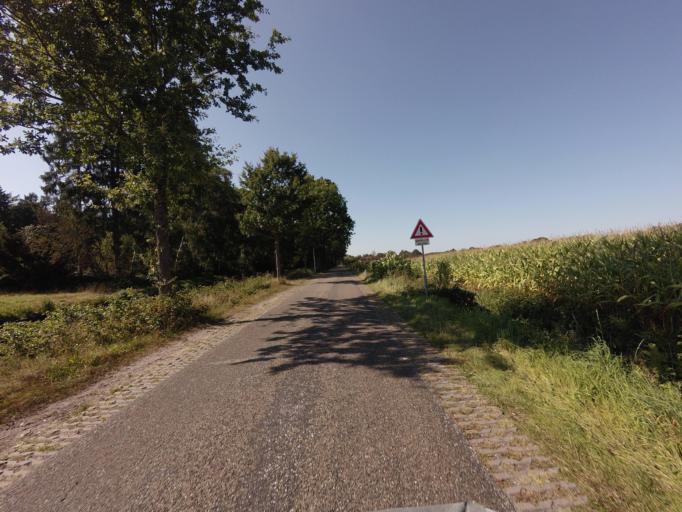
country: NL
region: Overijssel
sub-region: Gemeente Hardenberg
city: Hardenberg
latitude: 52.5324
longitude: 6.6386
